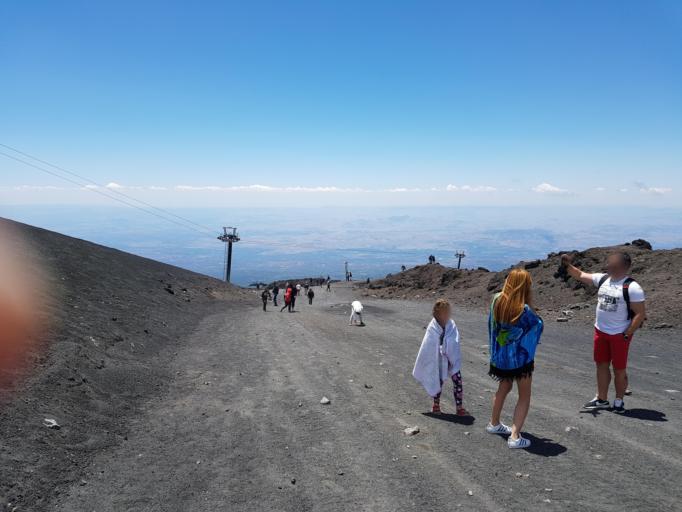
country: IT
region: Sicily
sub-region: Catania
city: Ragalna
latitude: 37.7119
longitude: 14.9950
